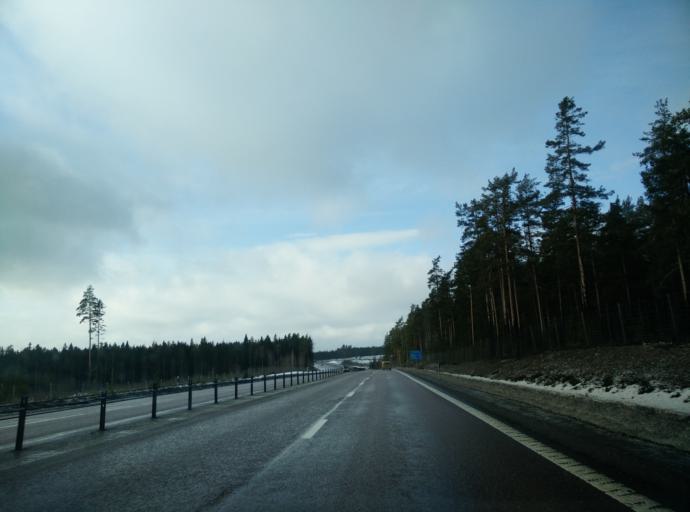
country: SE
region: Gaevleborg
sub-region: Sandvikens Kommun
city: Sandviken
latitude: 60.6197
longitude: 16.7061
